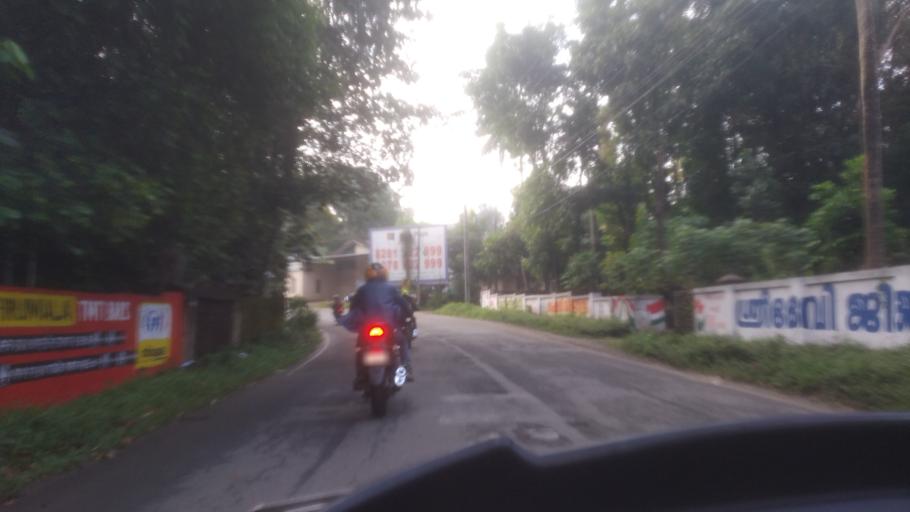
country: IN
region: Kerala
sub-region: Ernakulam
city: Perumpavur
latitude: 10.1061
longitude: 76.5361
